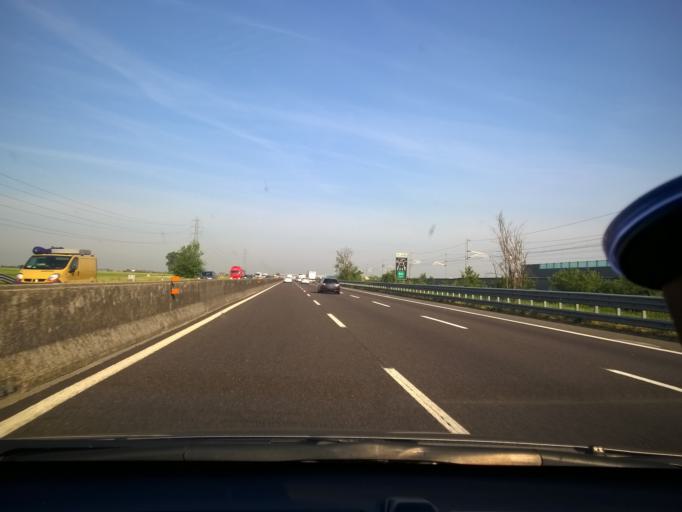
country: IT
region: Emilia-Romagna
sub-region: Provincia di Reggio Emilia
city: Prato
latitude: 44.6975
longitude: 10.7586
